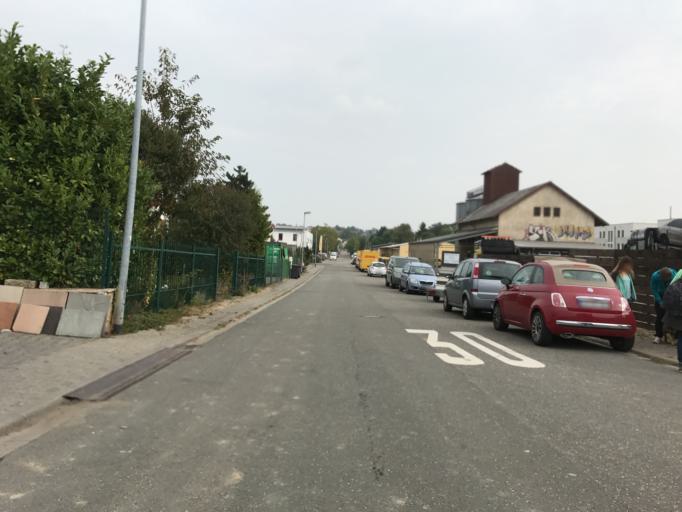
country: DE
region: Rheinland-Pfalz
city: Klein-Winternheim
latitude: 49.9403
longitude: 8.2073
